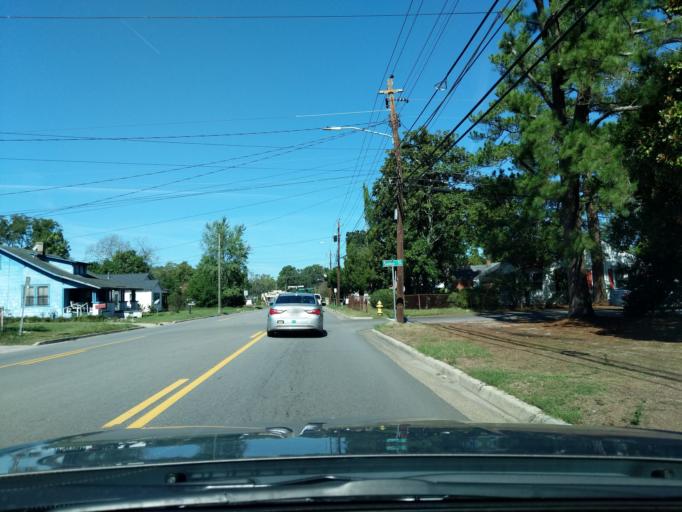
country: US
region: Georgia
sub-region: Richmond County
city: Augusta
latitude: 33.4461
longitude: -82.0058
